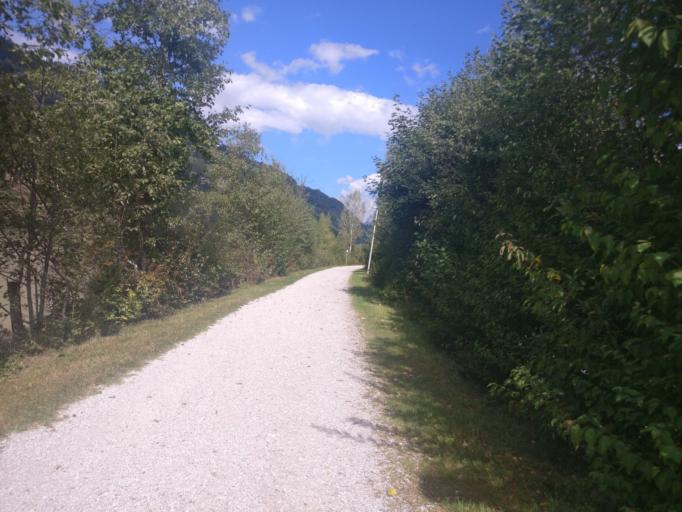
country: AT
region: Salzburg
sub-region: Politischer Bezirk Sankt Johann im Pongau
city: Sankt Johann im Pongau
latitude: 47.3645
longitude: 13.2082
